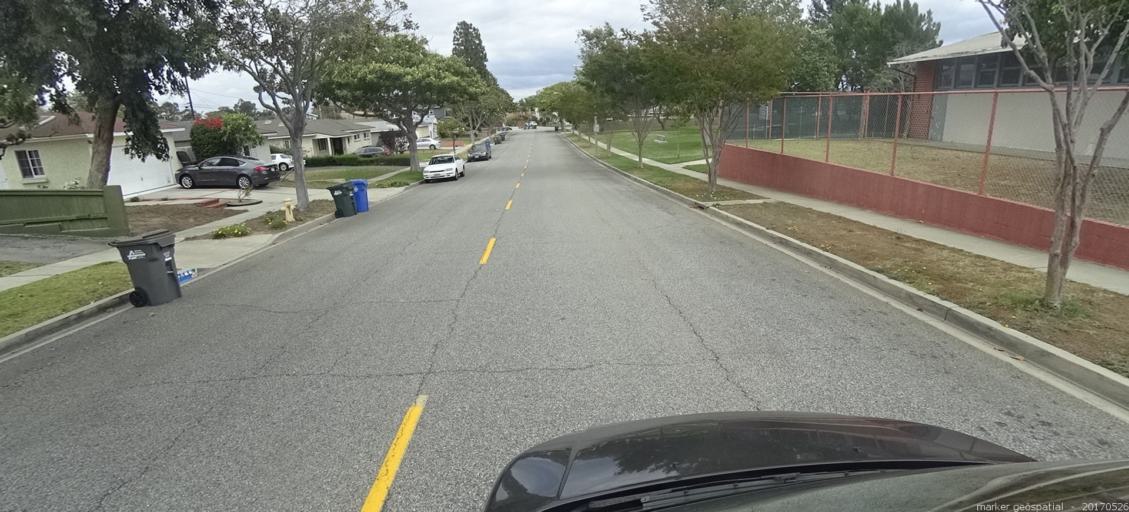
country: US
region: California
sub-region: Los Angeles County
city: Lawndale
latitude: 33.8620
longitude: -118.3603
